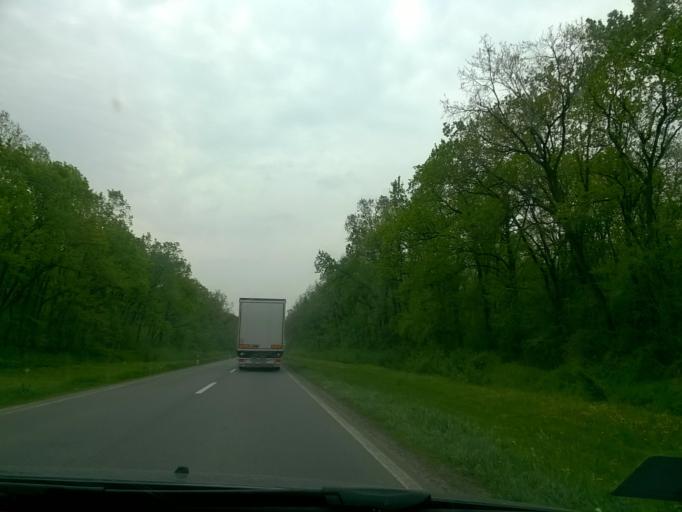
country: RS
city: Hrtkovci
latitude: 44.8978
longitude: 19.7642
